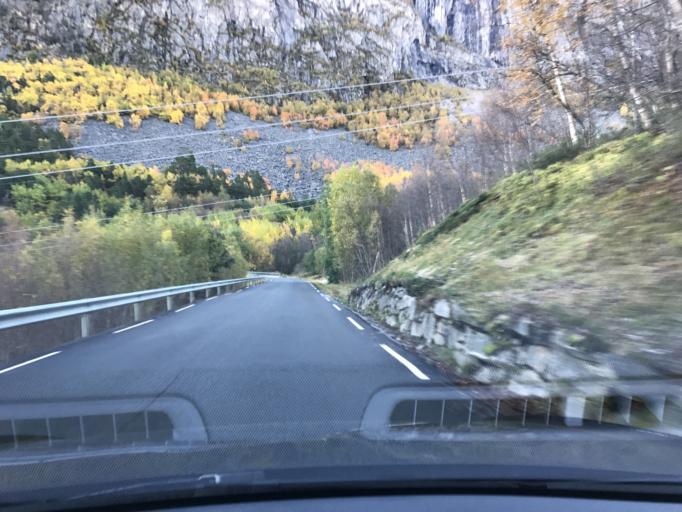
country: NO
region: Sogn og Fjordane
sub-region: Aurland
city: Aurlandsvangen
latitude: 60.8553
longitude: 7.3080
